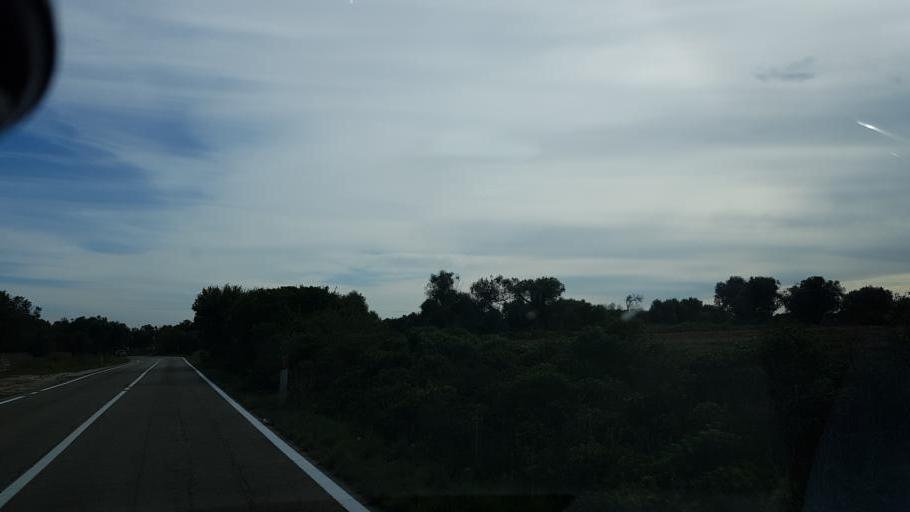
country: IT
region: Apulia
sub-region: Provincia di Lecce
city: Vernole
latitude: 40.3297
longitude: 18.3410
